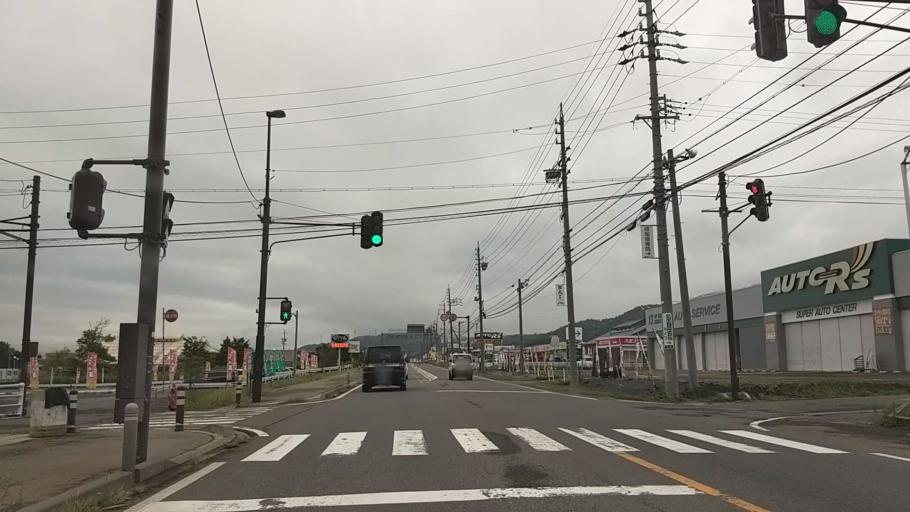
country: JP
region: Nagano
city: Iiyama
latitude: 36.8350
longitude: 138.3575
